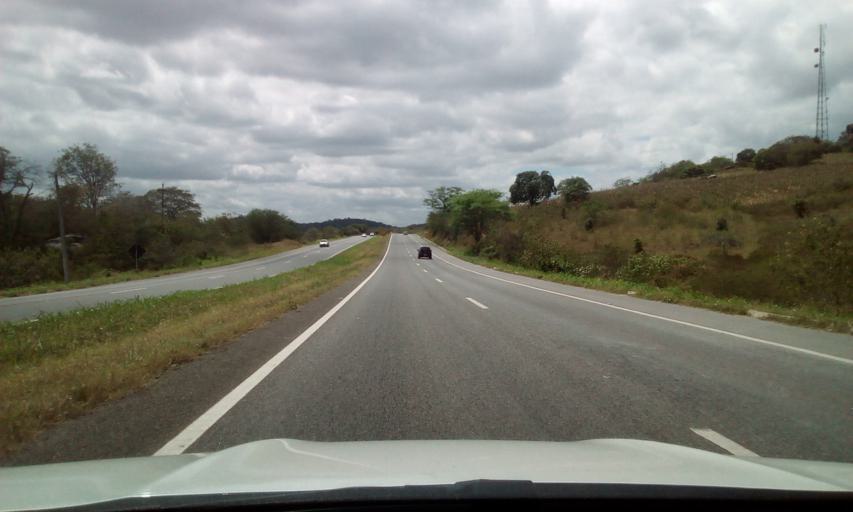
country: BR
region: Paraiba
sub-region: Massaranduba
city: Massaranduba
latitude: -7.2695
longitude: -35.7907
